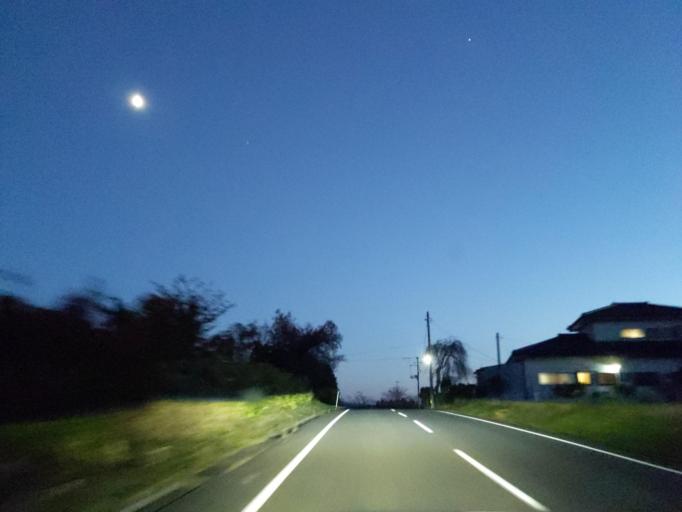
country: JP
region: Fukushima
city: Sukagawa
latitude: 37.3323
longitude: 140.3867
